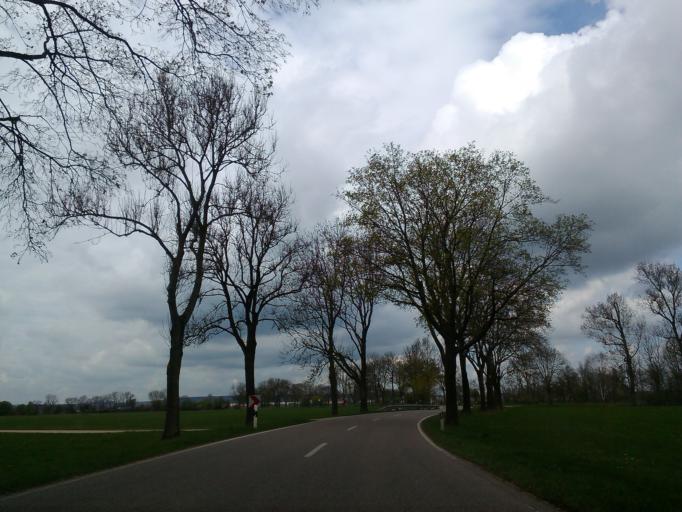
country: DE
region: Baden-Wuerttemberg
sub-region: Tuebingen Region
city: Langenau
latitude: 48.4805
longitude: 10.1477
